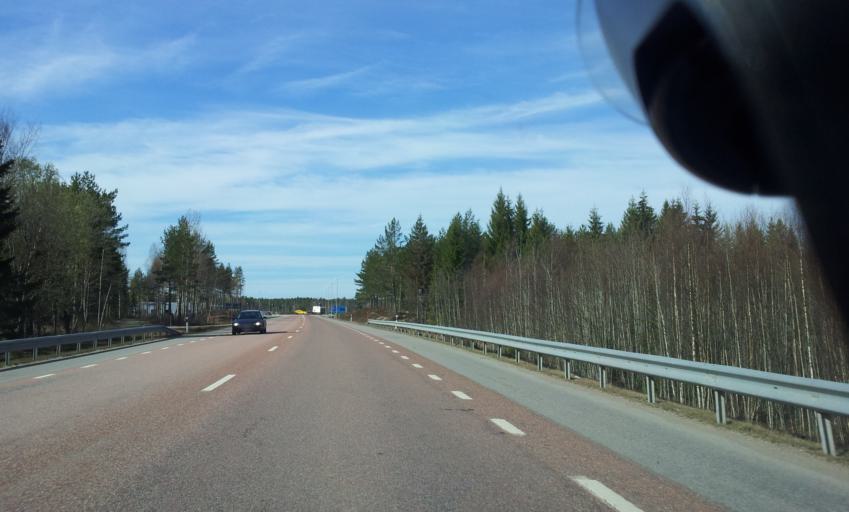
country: SE
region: Gaevleborg
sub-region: Hudiksvalls Kommun
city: Hudiksvall
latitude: 61.7149
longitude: 17.0575
